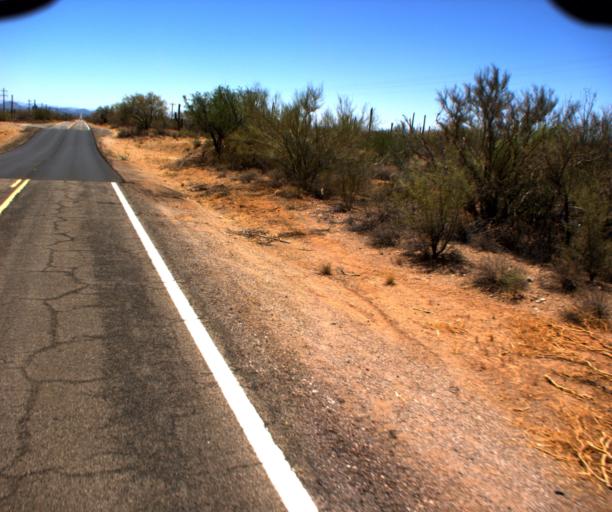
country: US
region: Arizona
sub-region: Pima County
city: Sells
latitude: 32.1407
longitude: -112.0981
